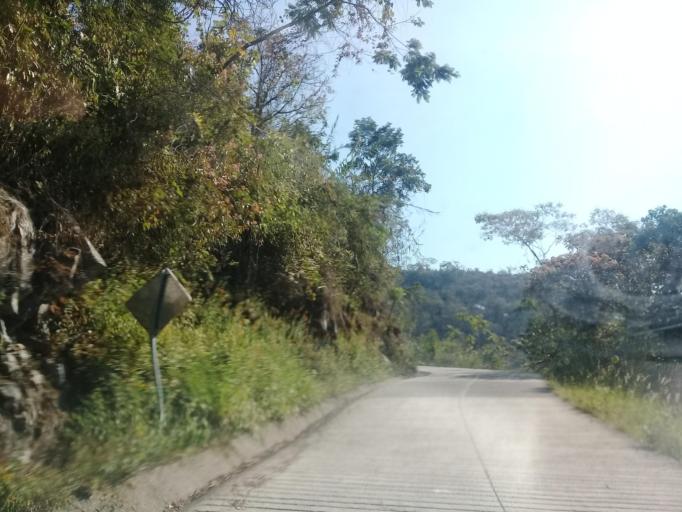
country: MX
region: Veracruz
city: Rafael Delgado
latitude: 18.7819
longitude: -97.0253
